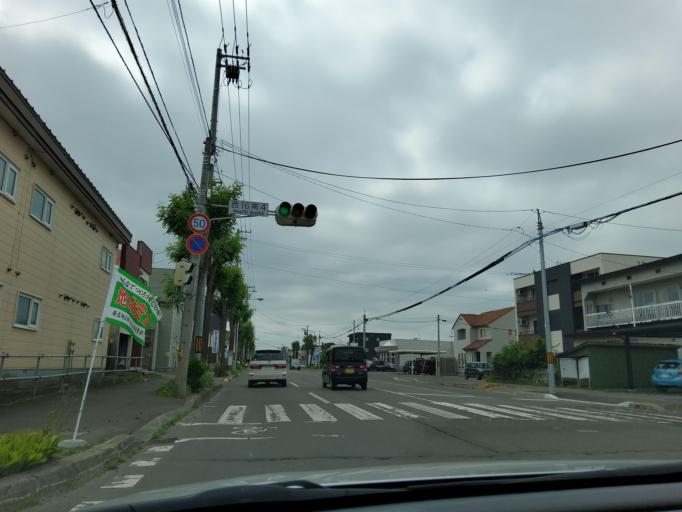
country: JP
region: Hokkaido
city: Obihiro
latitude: 42.9148
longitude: 143.1761
